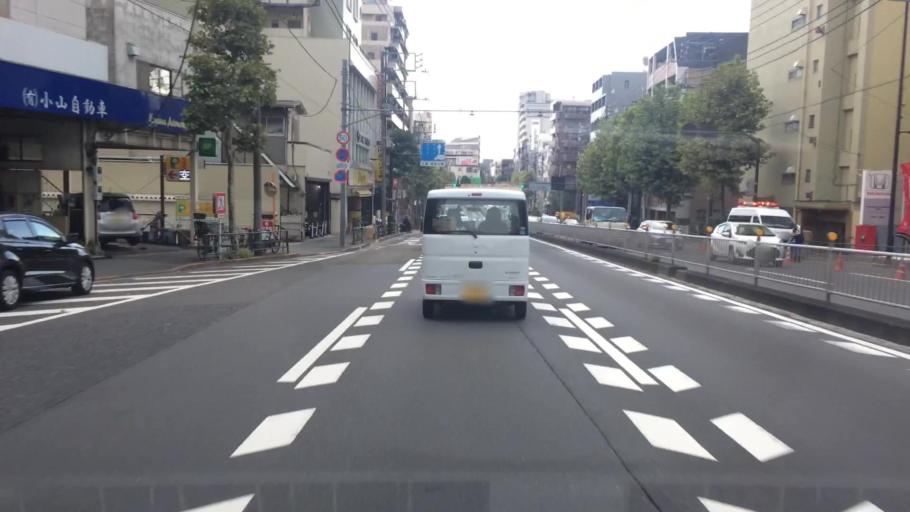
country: JP
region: Tokyo
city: Tokyo
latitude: 35.6816
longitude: 139.6570
